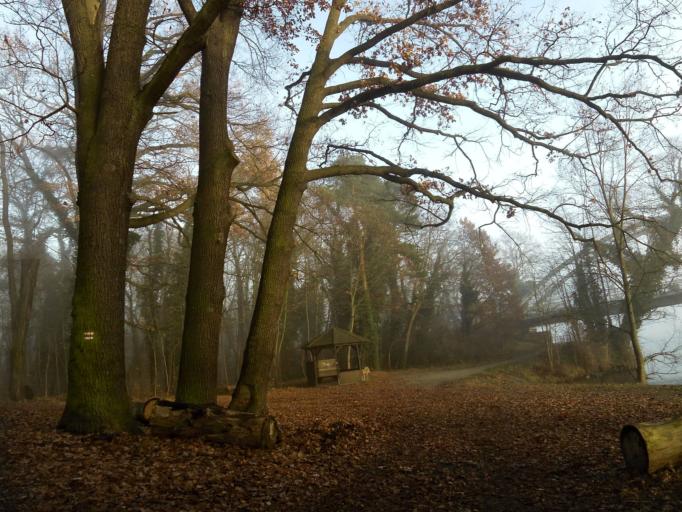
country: DE
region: Brandenburg
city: Michendorf
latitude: 52.3580
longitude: 12.9950
